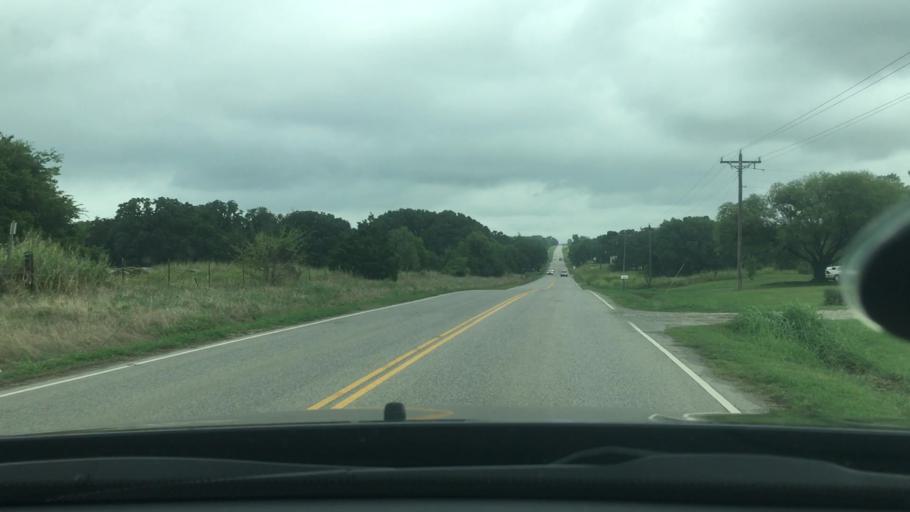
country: US
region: Oklahoma
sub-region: Bryan County
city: Calera
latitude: 33.9376
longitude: -96.5005
